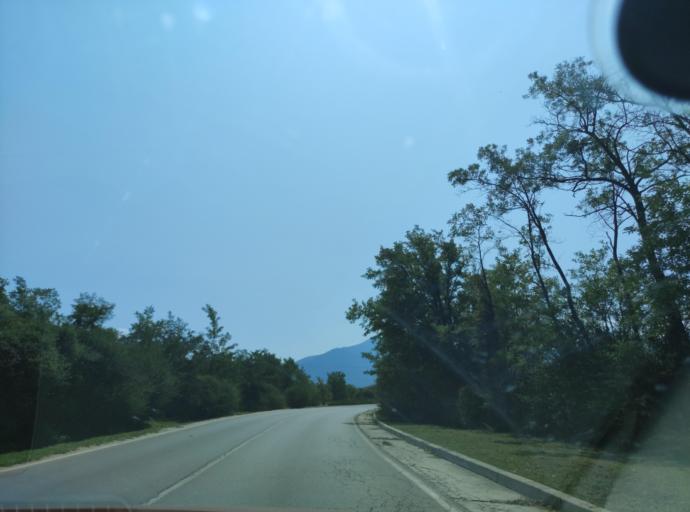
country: BG
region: Blagoevgrad
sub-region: Obshtina Razlog
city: Razlog
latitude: 41.8709
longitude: 23.4762
